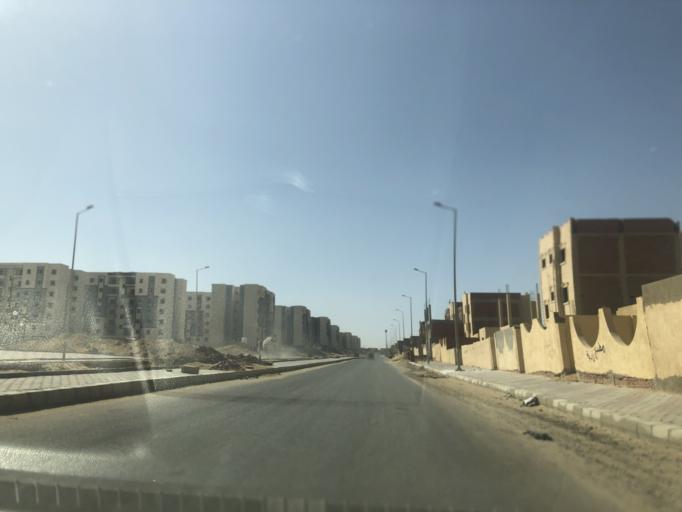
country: EG
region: Al Jizah
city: Madinat Sittah Uktubar
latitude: 29.9314
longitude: 30.9867
